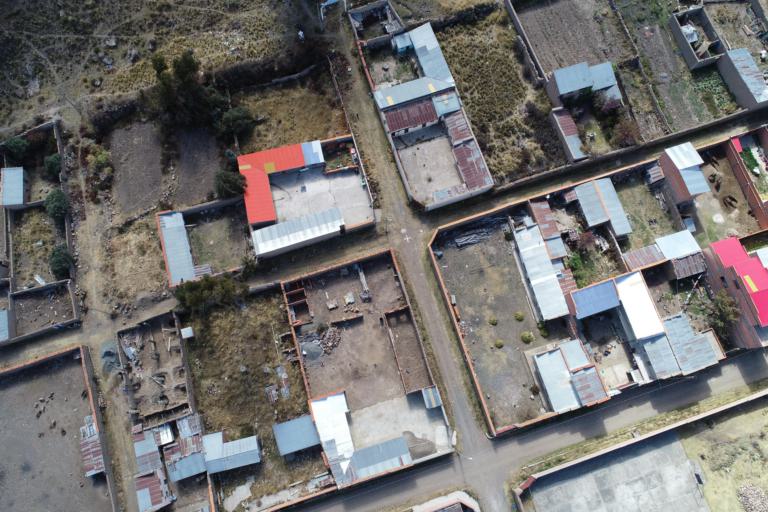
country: BO
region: La Paz
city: Achacachi
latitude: -15.8962
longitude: -68.9055
